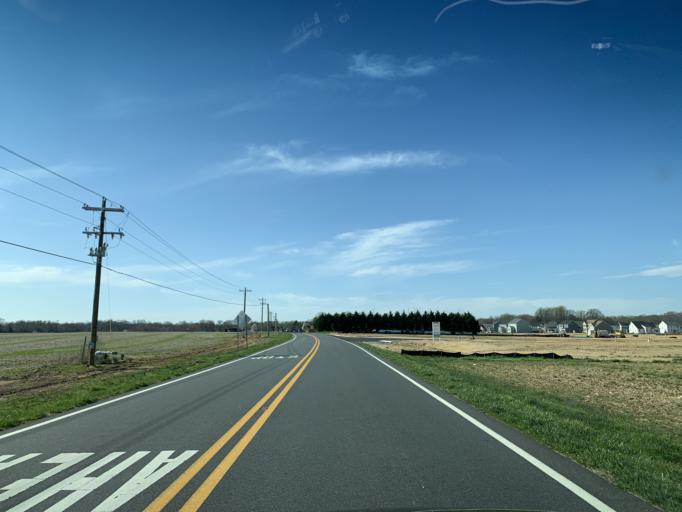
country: US
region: Delaware
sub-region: Kent County
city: Riverview
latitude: 38.9798
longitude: -75.5020
